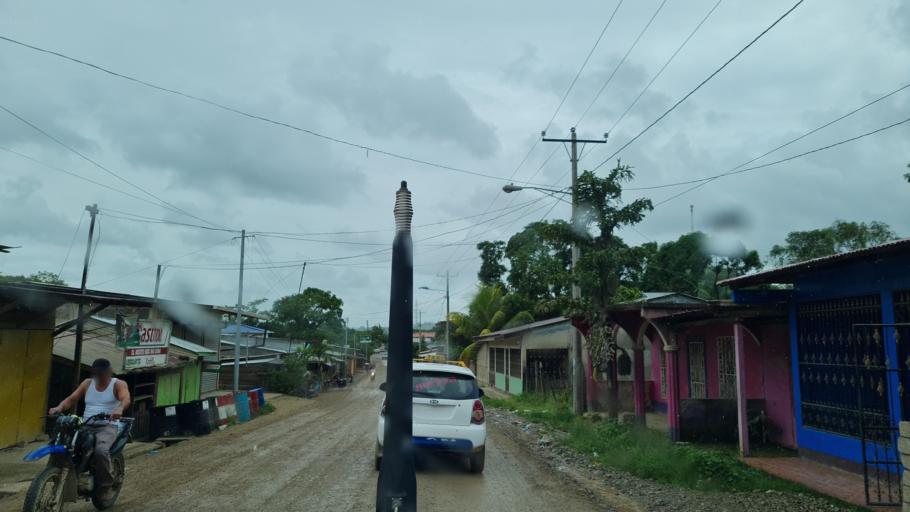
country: NI
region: Atlantico Norte (RAAN)
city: Bonanza
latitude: 13.9217
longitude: -84.3932
